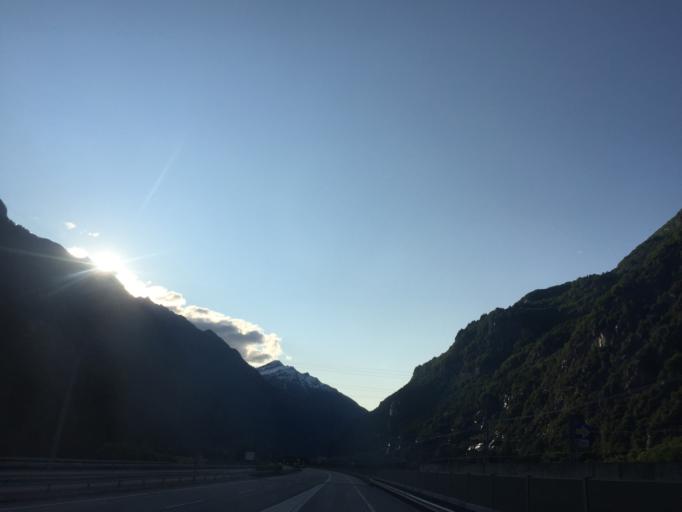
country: CH
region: Ticino
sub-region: Riviera District
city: Biasca
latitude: 46.3574
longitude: 8.9547
